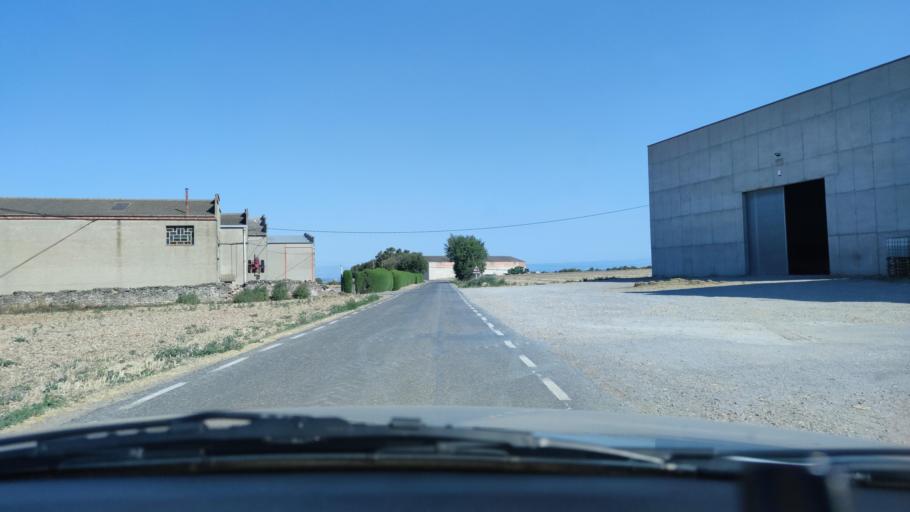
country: ES
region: Catalonia
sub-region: Provincia de Lleida
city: Ivorra
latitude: 41.7295
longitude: 1.3659
